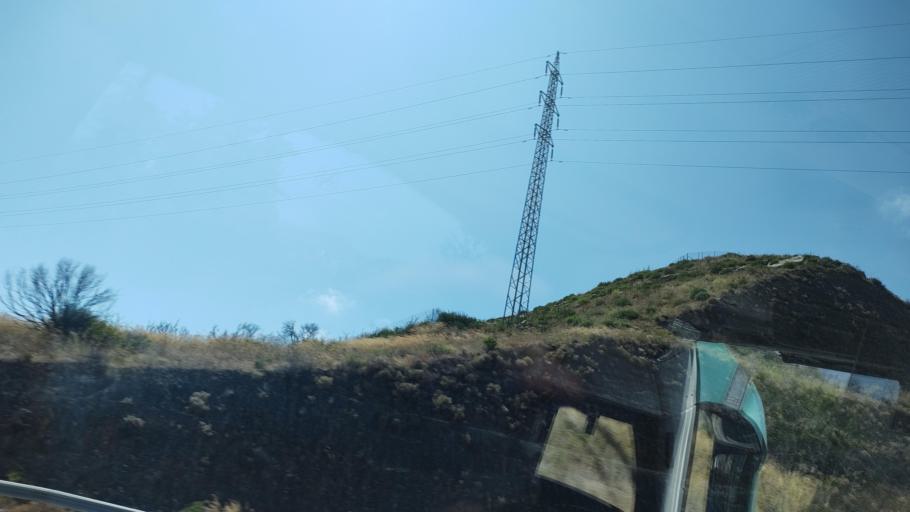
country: ES
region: Andalusia
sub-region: Provincia de Malaga
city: Manilva
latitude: 36.3461
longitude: -5.2705
